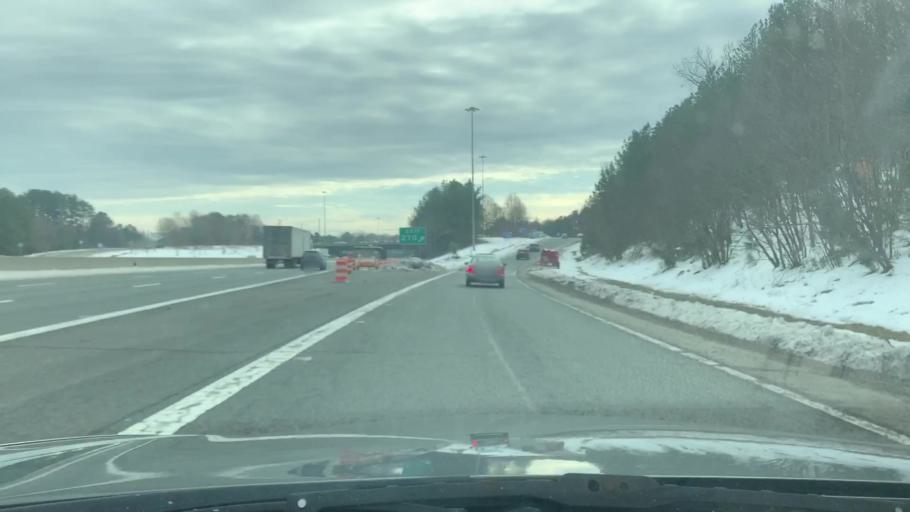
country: US
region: North Carolina
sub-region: Orange County
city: Chapel Hill
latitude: 35.9532
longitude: -79.0018
